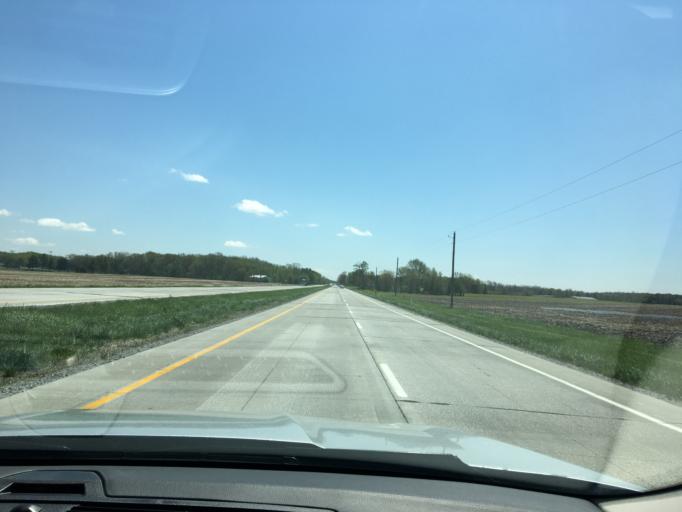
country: US
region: Indiana
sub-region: Tippecanoe County
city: Dayton
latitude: 40.3157
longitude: -86.7665
